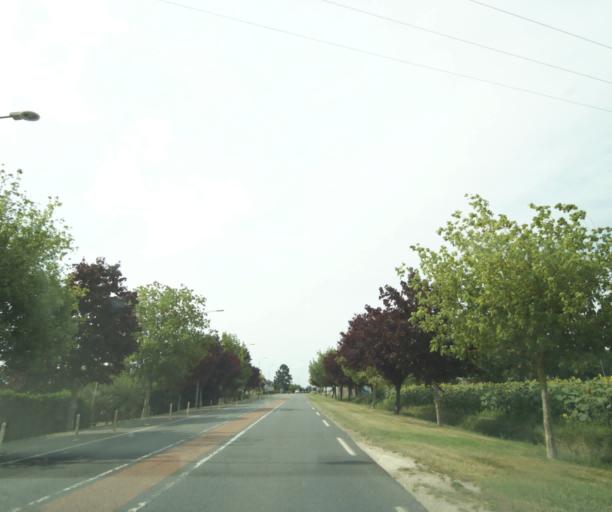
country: FR
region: Centre
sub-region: Departement d'Indre-et-Loire
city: Neuille-Pont-Pierre
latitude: 47.5433
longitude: 0.5539
